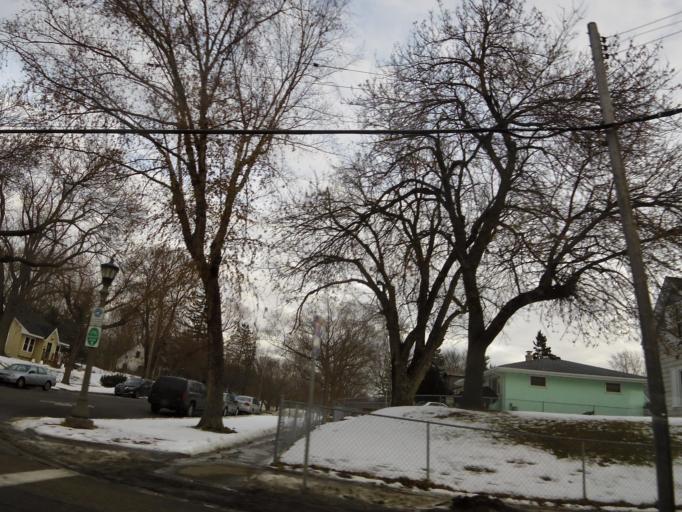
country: US
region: Minnesota
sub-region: Ramsey County
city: Maplewood
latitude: 44.9612
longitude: -93.0151
